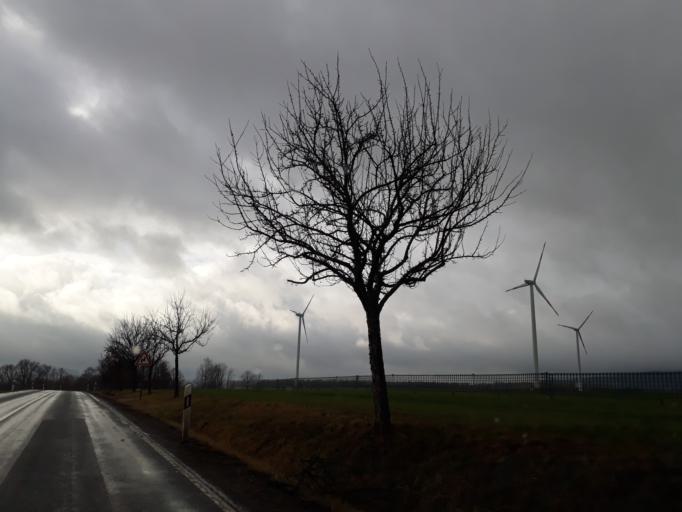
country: DE
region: Saxony
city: Herrnhut
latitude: 51.0124
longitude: 14.7314
